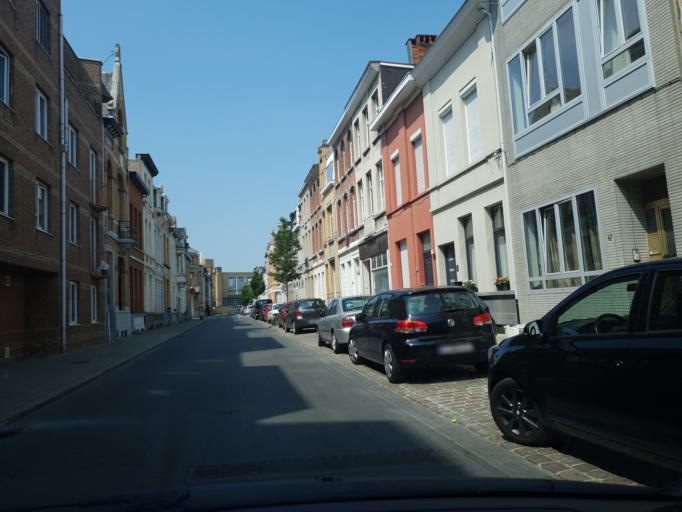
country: BE
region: Flanders
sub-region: Provincie Antwerpen
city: Borsbeek
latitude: 51.2214
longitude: 4.4647
